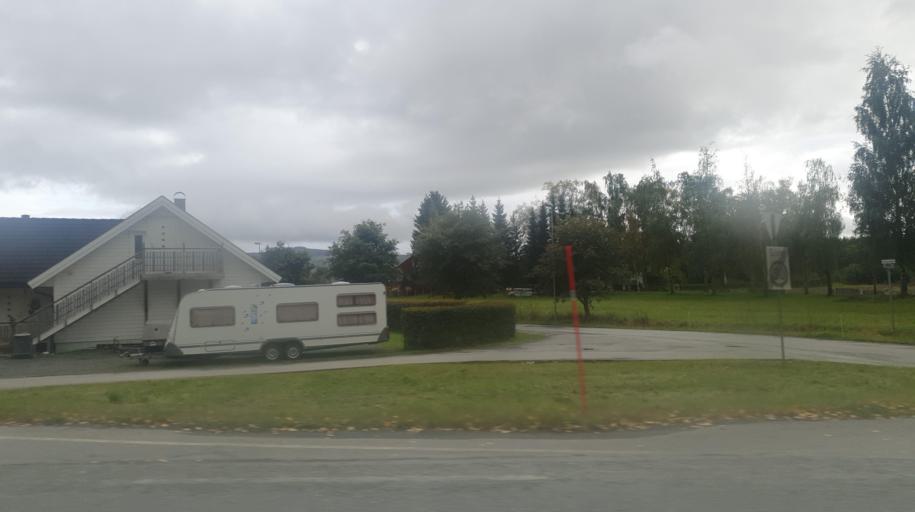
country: NO
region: Nord-Trondelag
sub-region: Verdal
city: Verdal
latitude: 63.7956
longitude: 11.5094
